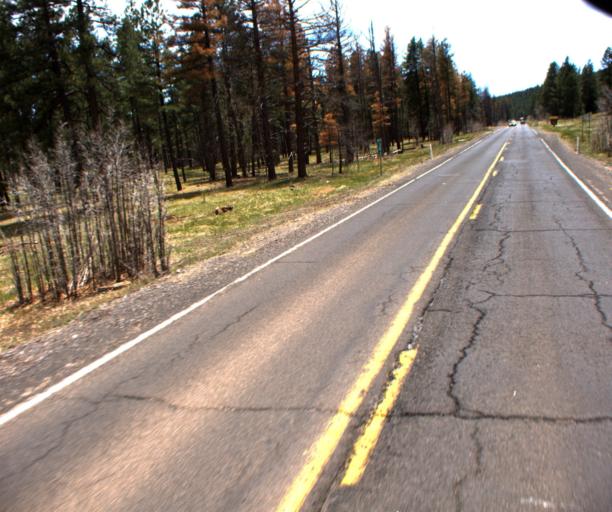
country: US
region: Arizona
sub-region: Coconino County
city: Kachina Village
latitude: 35.0735
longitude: -111.7309
